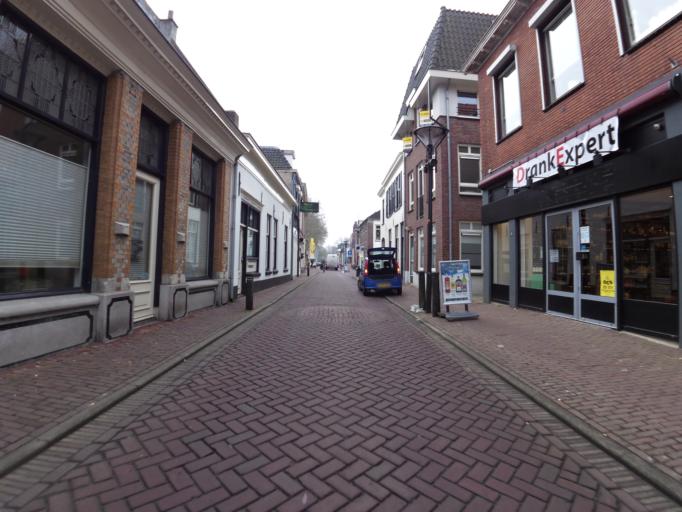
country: NL
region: Gelderland
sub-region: Gemeente Zevenaar
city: Zevenaar
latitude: 51.9258
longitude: 6.0750
